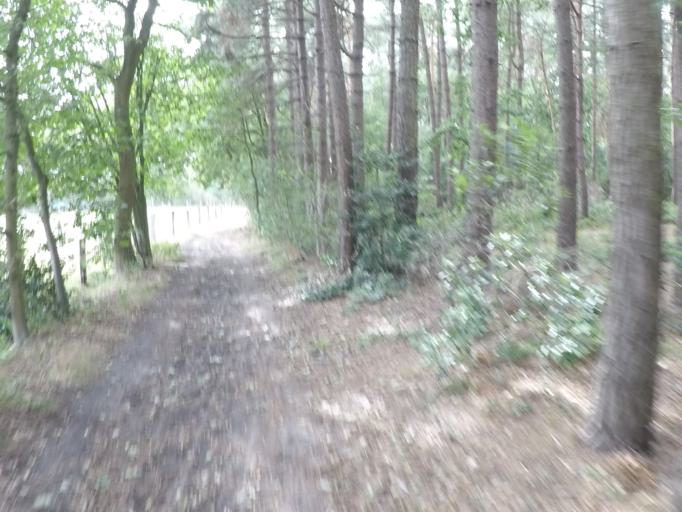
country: BE
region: Flanders
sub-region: Provincie Antwerpen
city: Vorselaar
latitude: 51.2191
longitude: 4.7645
